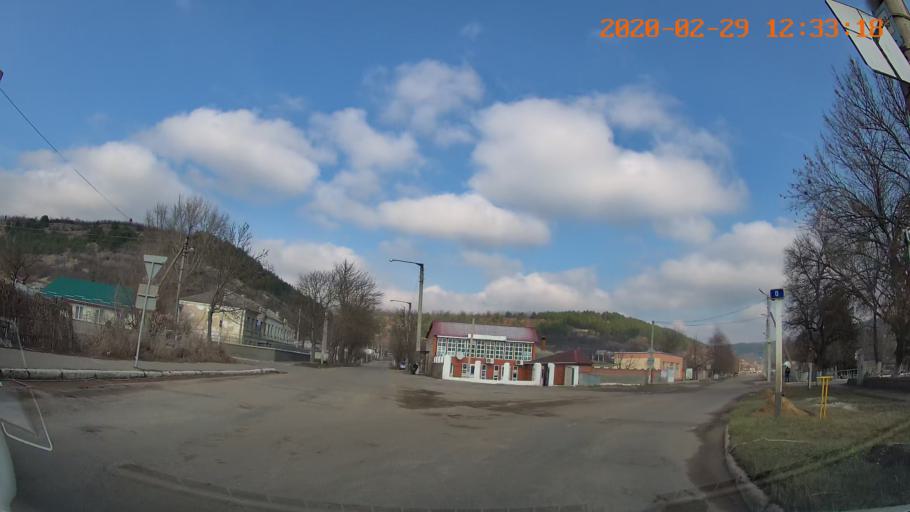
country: MD
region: Telenesti
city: Camenca
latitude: 48.0346
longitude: 28.7035
